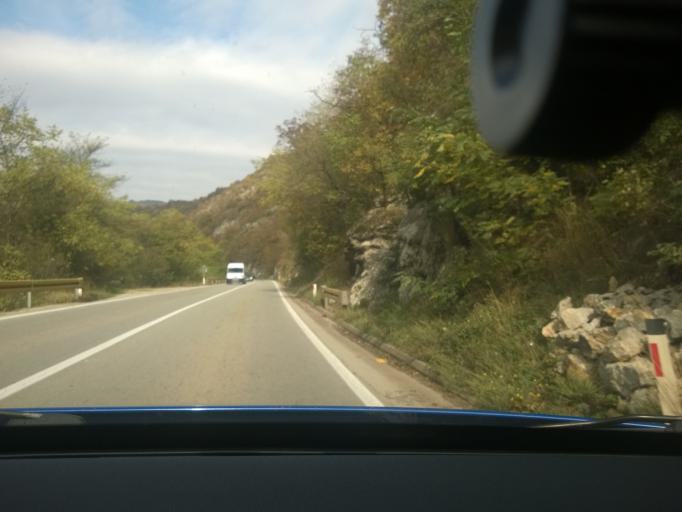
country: RS
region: Central Serbia
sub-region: Nisavski Okrug
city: Svrljig
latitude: 43.3291
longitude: 22.0999
